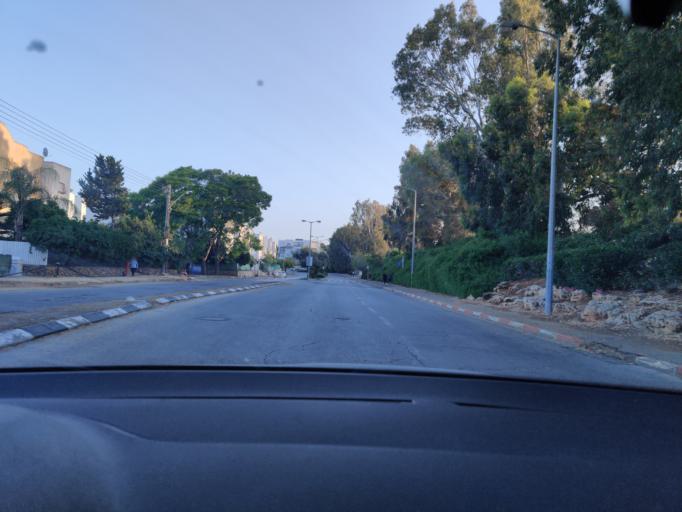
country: IL
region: Haifa
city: Hadera
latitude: 32.4766
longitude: 34.9527
